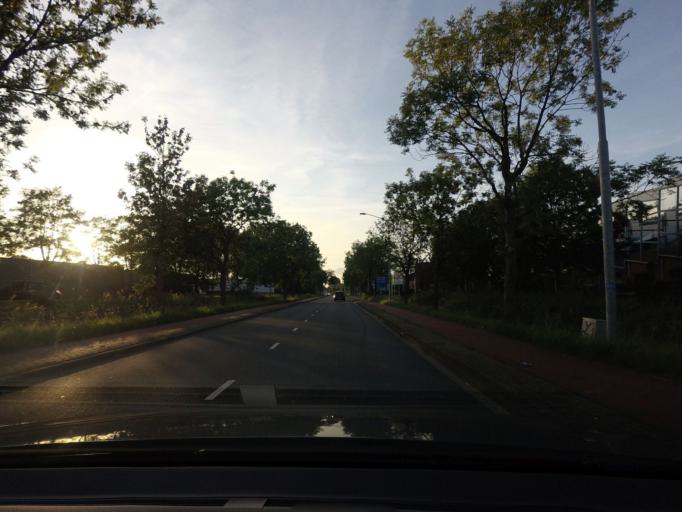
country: NL
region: North Holland
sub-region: Gemeente Alkmaar
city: Alkmaar
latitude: 52.6290
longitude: 4.7668
